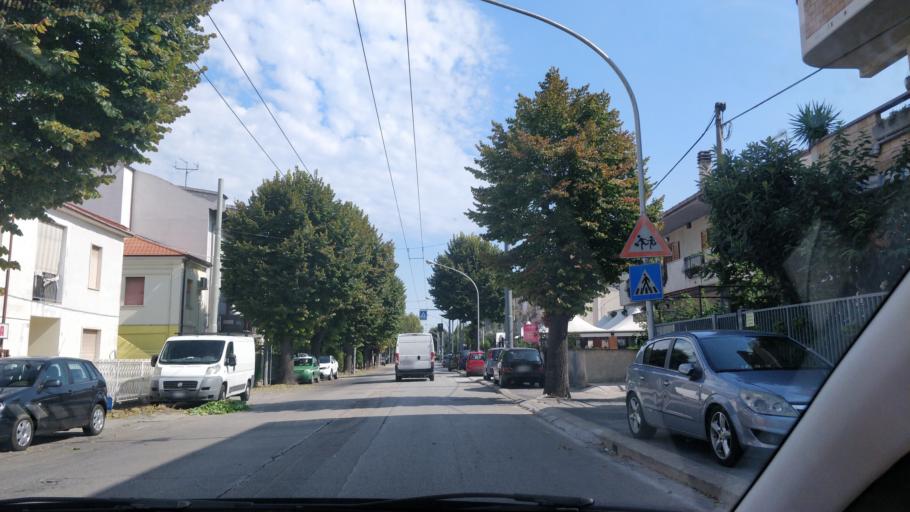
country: IT
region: Abruzzo
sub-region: Provincia di Chieti
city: Chieti
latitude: 42.3785
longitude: 14.1478
